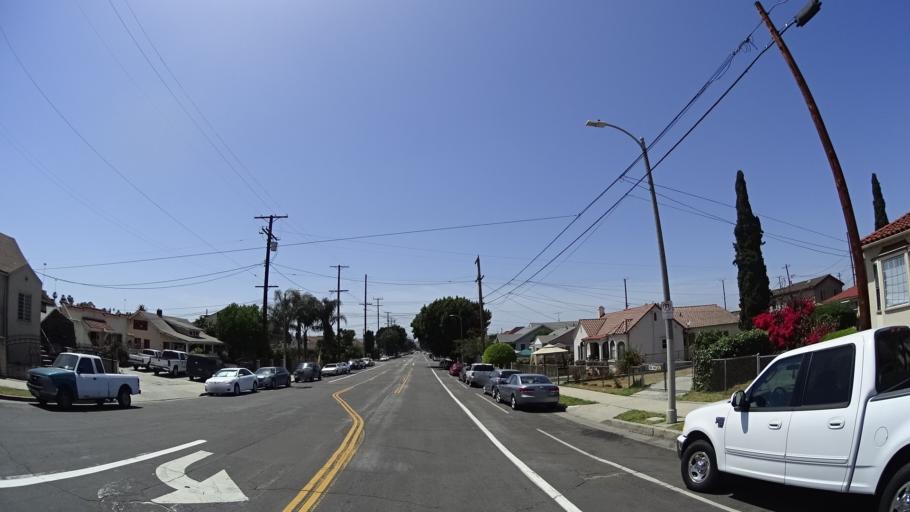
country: US
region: California
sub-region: Los Angeles County
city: Boyle Heights
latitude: 34.0677
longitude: -118.2053
